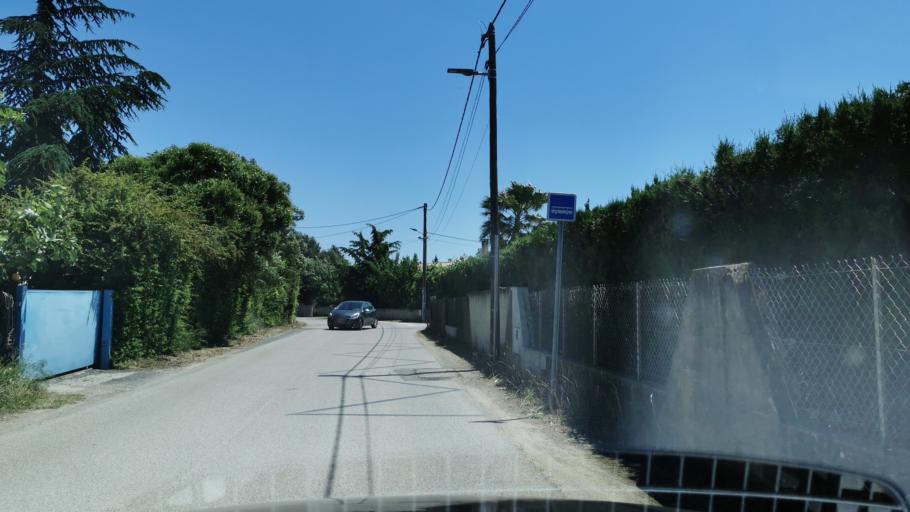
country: FR
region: Languedoc-Roussillon
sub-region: Departement de l'Aude
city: Ouveillan
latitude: 43.2599
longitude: 3.0118
